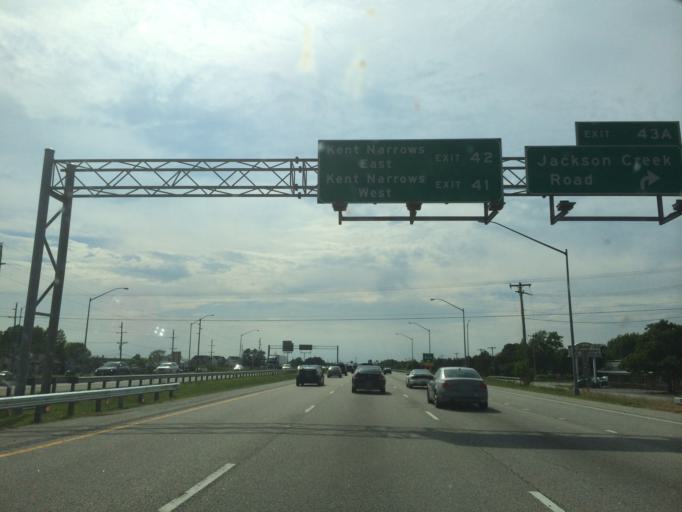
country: US
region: Maryland
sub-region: Queen Anne's County
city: Grasonville
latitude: 38.9646
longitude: -76.2197
